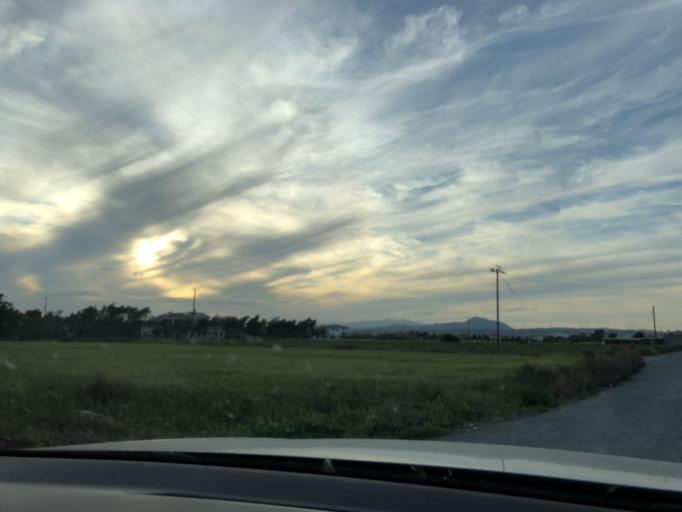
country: CY
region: Larnaka
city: Perivolia
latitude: 34.8294
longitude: 33.6025
